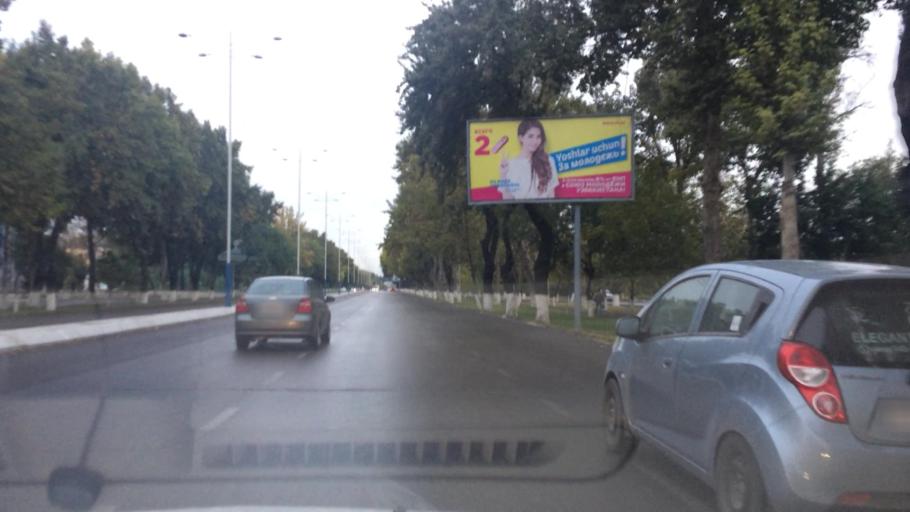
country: UZ
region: Toshkent Shahri
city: Tashkent
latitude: 41.2642
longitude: 69.1986
